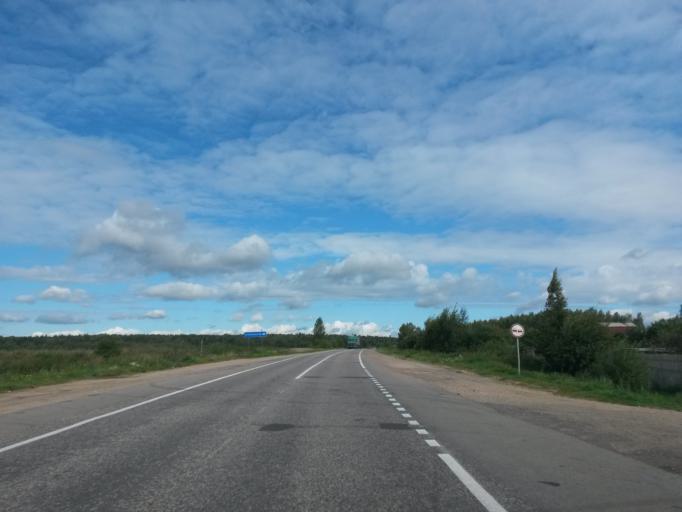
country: RU
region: Jaroslavl
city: Krasnyye Tkachi
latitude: 57.4600
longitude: 39.9092
